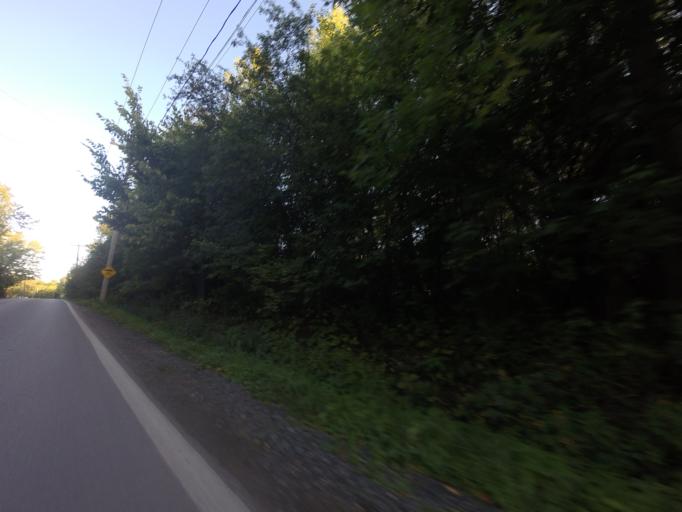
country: CA
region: Quebec
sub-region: Monteregie
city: Hudson
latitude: 45.4716
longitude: -74.1798
